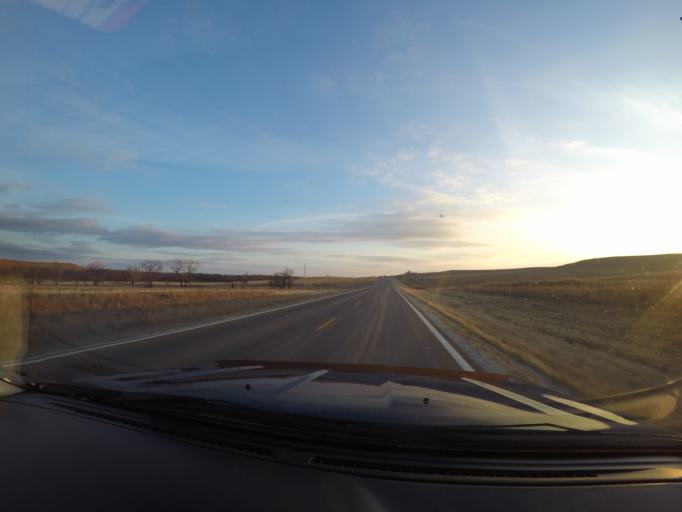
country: US
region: Kansas
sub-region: Chase County
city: Cottonwood Falls
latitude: 38.4193
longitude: -96.5571
